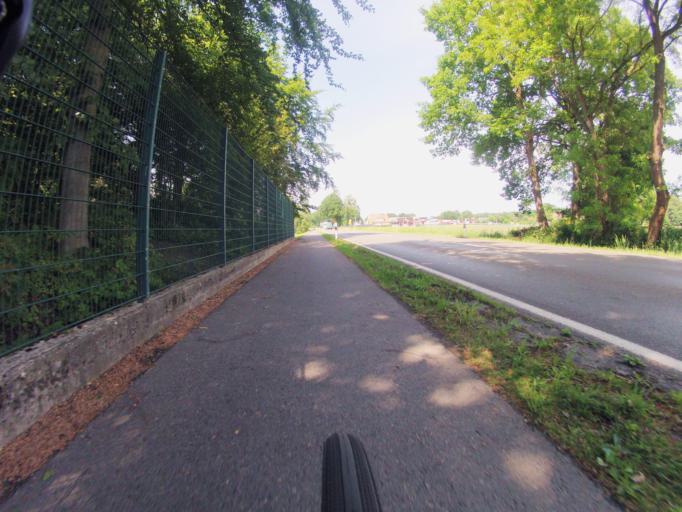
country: DE
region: North Rhine-Westphalia
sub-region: Regierungsbezirk Munster
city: Horstel
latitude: 52.3085
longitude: 7.6341
